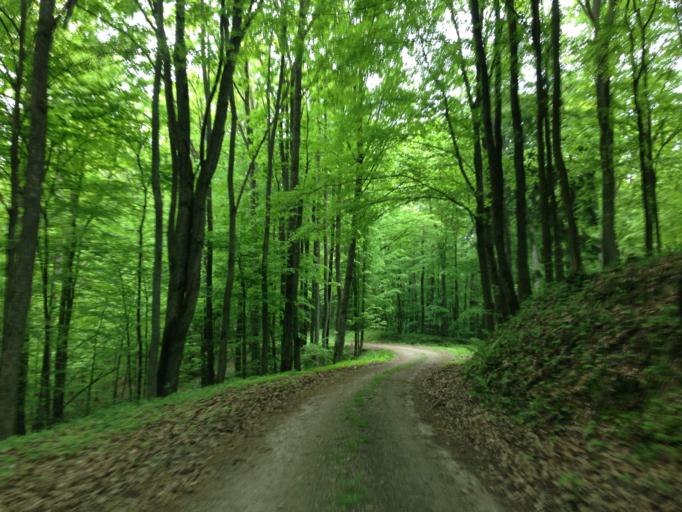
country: PL
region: Kujawsko-Pomorskie
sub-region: Powiat brodnicki
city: Gorzno
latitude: 53.2574
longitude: 19.7100
